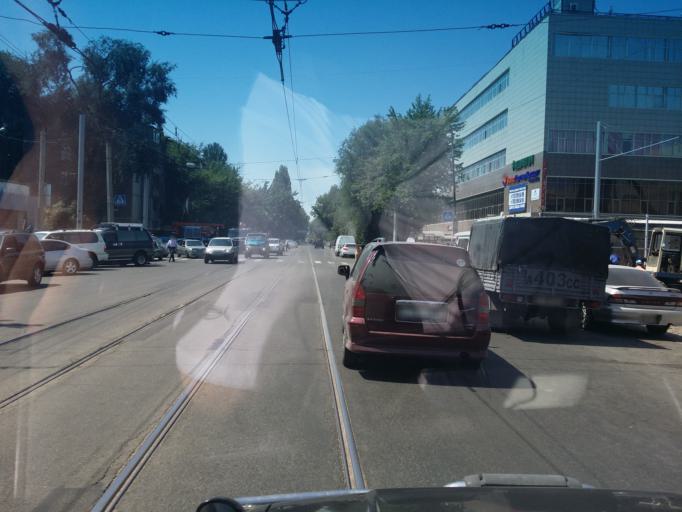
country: KZ
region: Almaty Qalasy
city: Almaty
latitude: 43.2628
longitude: 76.9287
